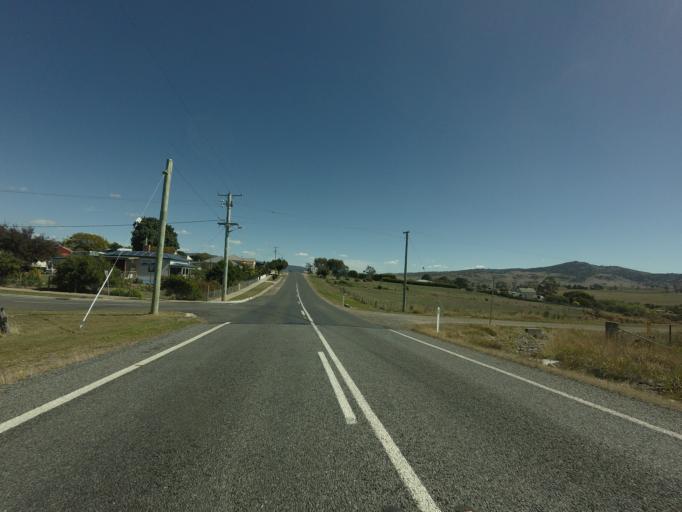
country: AU
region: Tasmania
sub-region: Northern Midlands
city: Evandale
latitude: -41.7797
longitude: 147.7252
